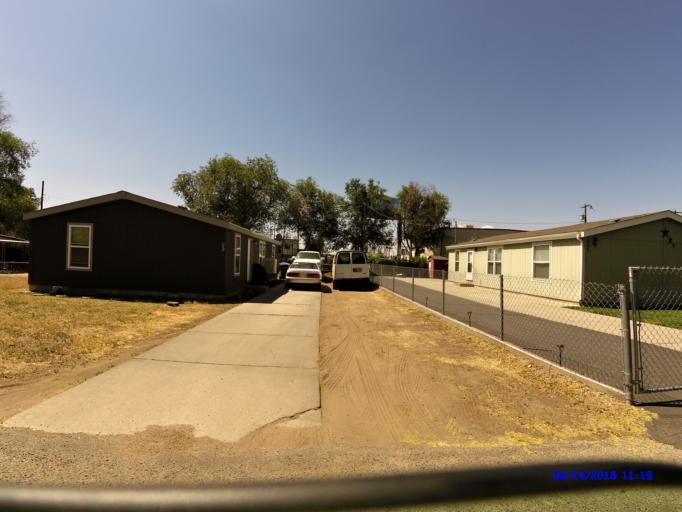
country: US
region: Utah
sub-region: Weber County
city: Ogden
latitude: 41.2159
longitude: -112.0002
